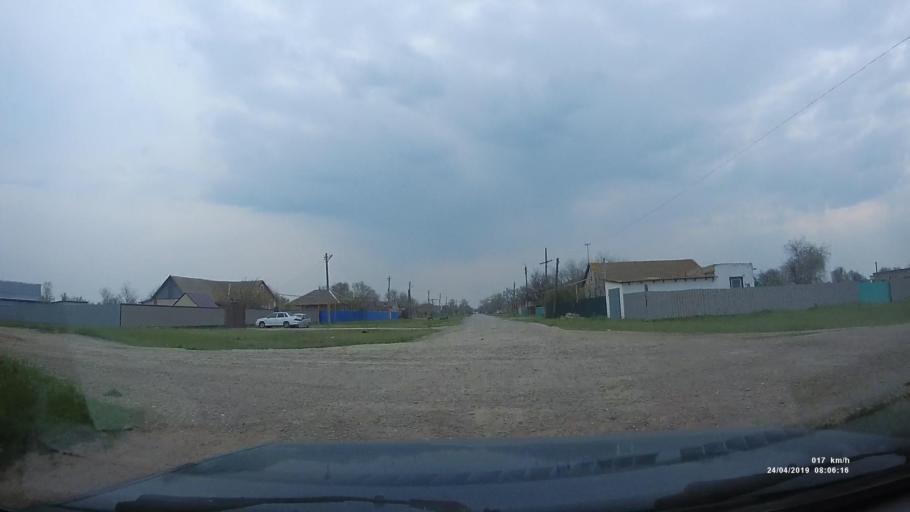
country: RU
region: Kalmykiya
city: Priyutnoye
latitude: 46.1007
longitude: 43.4910
